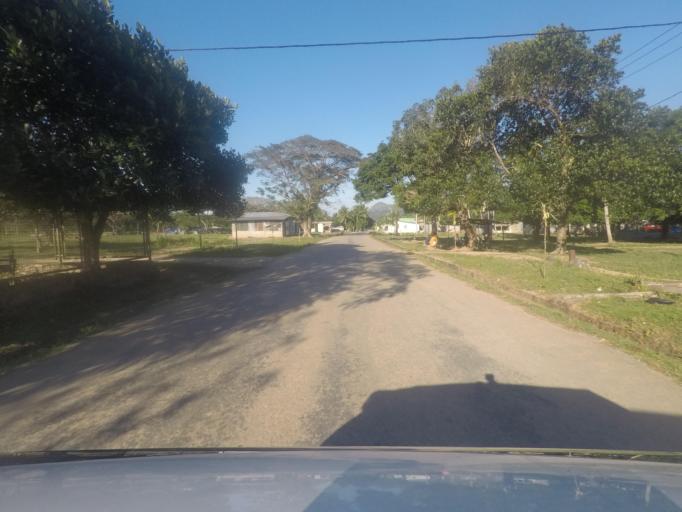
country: TL
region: Lautem
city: Lospalos
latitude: -8.3993
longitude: 127.1891
